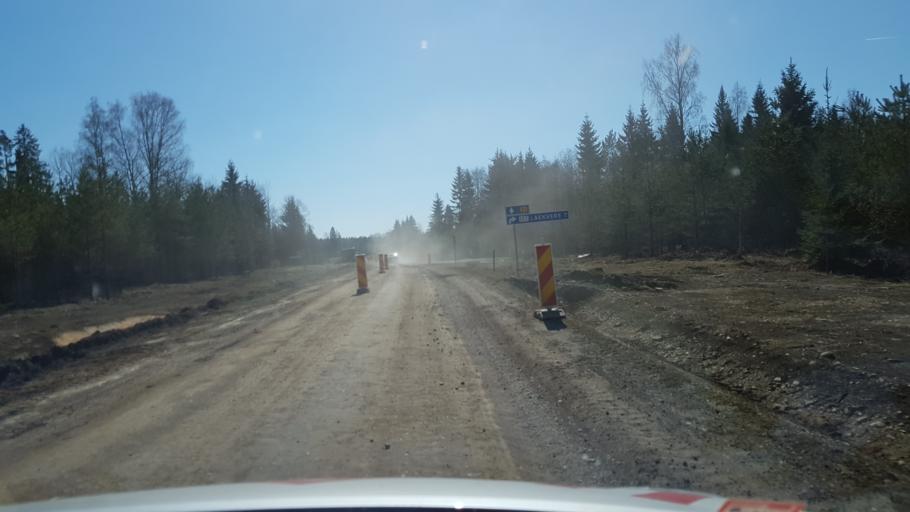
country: EE
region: Jogevamaa
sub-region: Mustvee linn
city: Mustvee
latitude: 59.0443
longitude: 26.6622
